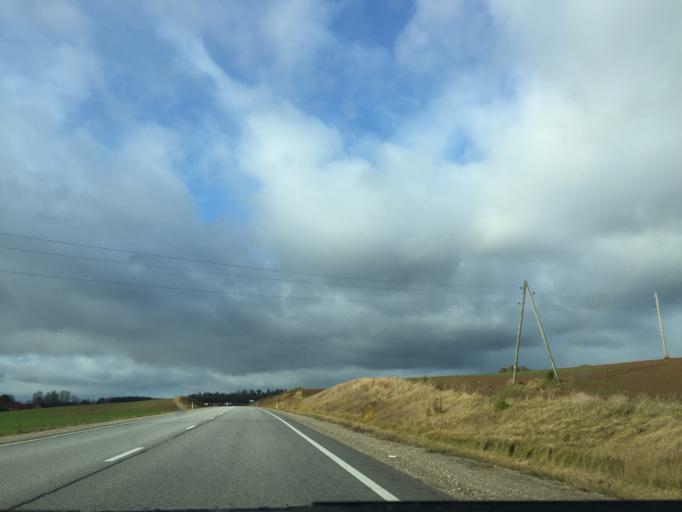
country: LV
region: Tukuma Rajons
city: Tukums
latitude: 56.9740
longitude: 23.0565
